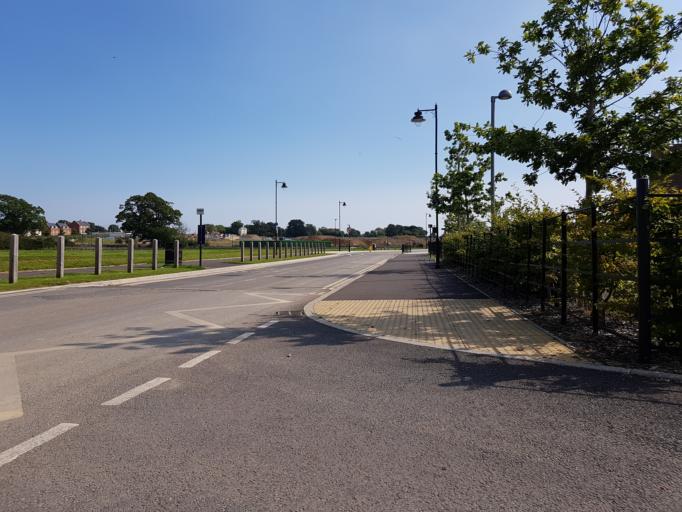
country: GB
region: England
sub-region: Hampshire
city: Waterlooville
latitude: 50.8818
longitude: -1.0461
